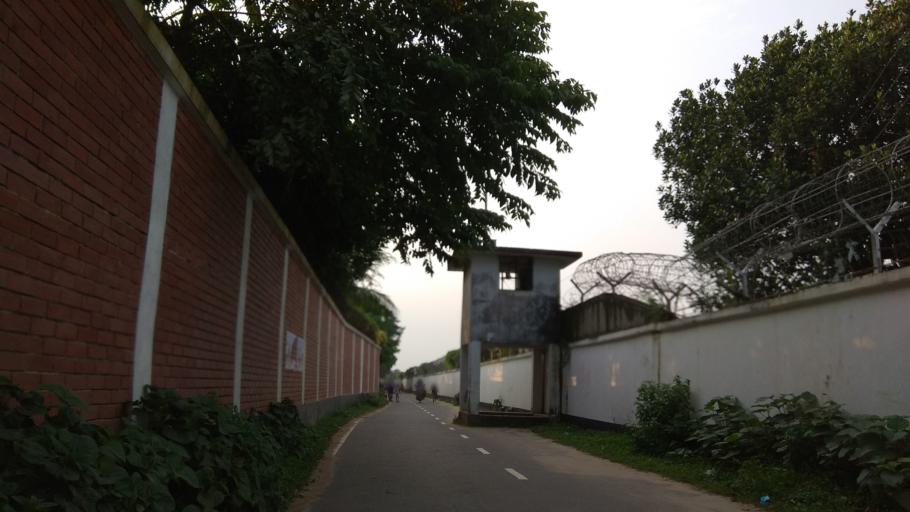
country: BD
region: Dhaka
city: Tungi
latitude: 23.8517
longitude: 90.3889
